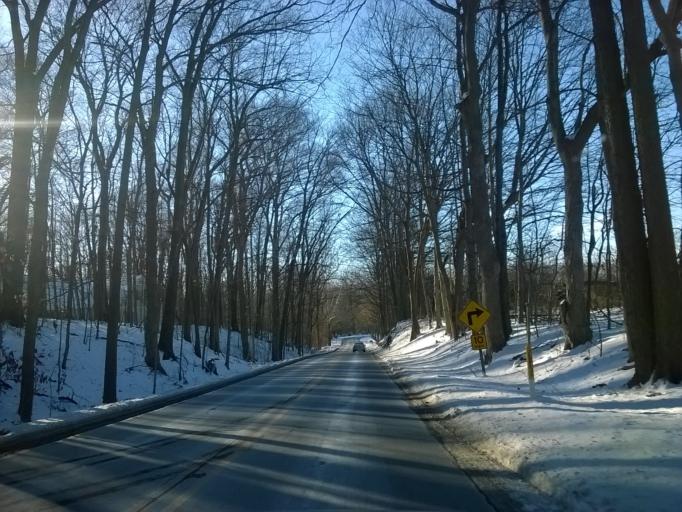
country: US
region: Indiana
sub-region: Boone County
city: Zionsville
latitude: 39.9248
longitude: -86.2757
